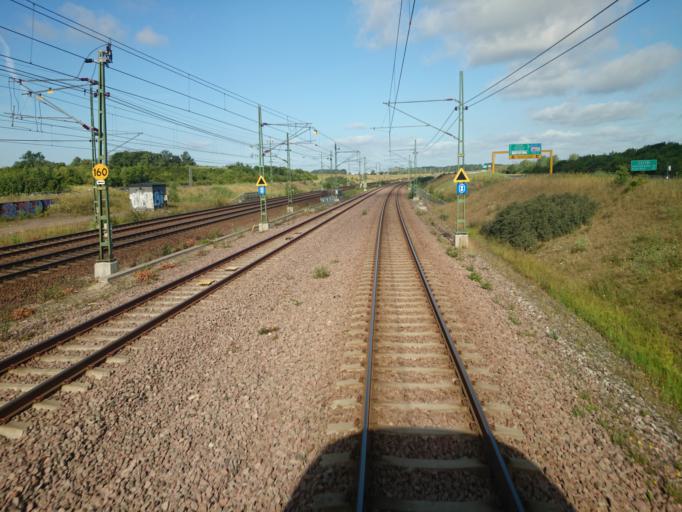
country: SE
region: Skane
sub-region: Malmo
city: Bunkeflostrand
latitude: 55.5472
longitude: 12.9710
